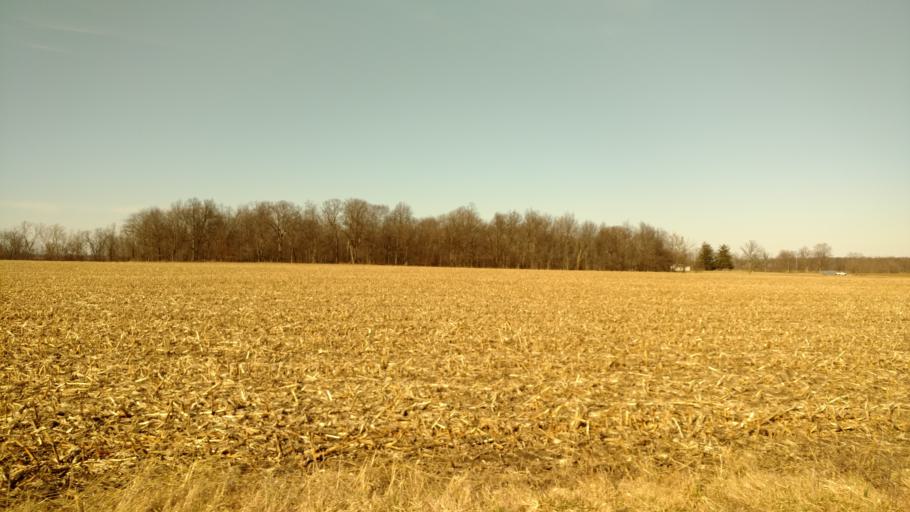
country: US
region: Ohio
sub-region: Marion County
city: Marion
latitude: 40.7029
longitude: -83.0771
